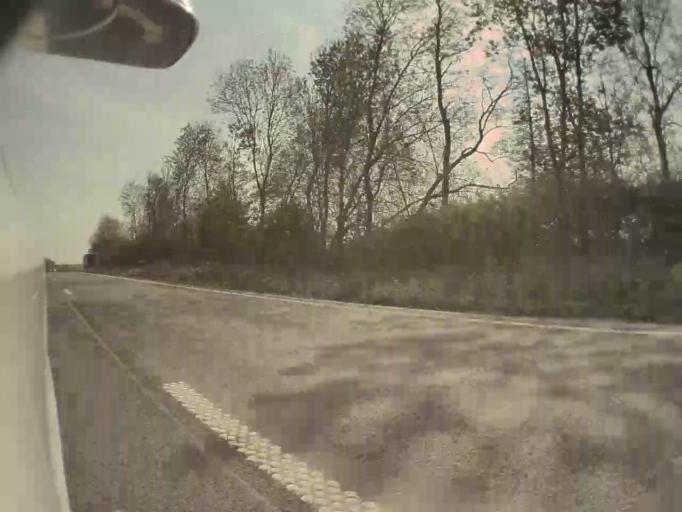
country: BE
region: Wallonia
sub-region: Province de Namur
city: Ciney
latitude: 50.3046
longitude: 5.1217
